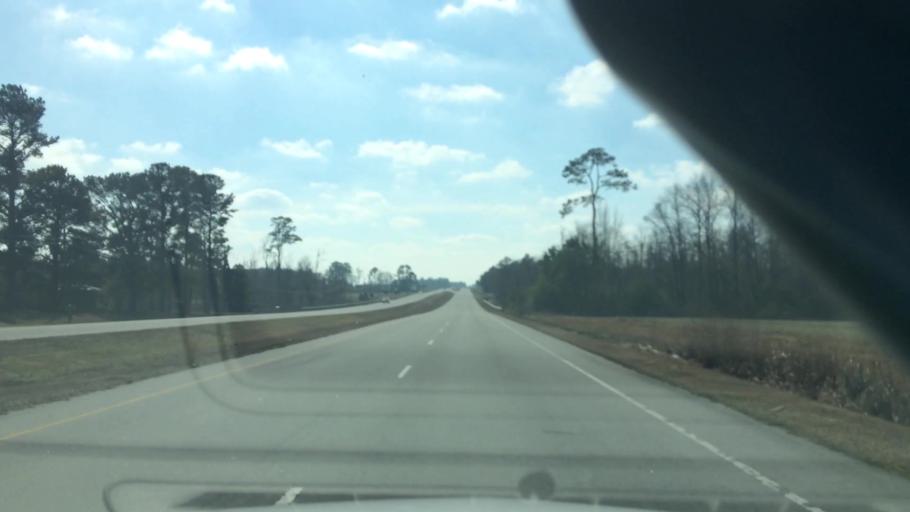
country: US
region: North Carolina
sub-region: Duplin County
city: Beulaville
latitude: 35.1086
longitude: -77.7200
